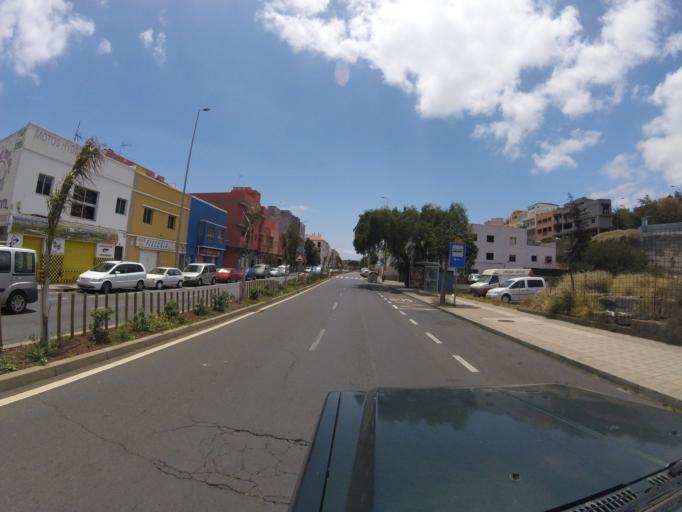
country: ES
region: Canary Islands
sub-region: Provincia de Santa Cruz de Tenerife
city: La Laguna
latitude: 28.4435
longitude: -16.3011
